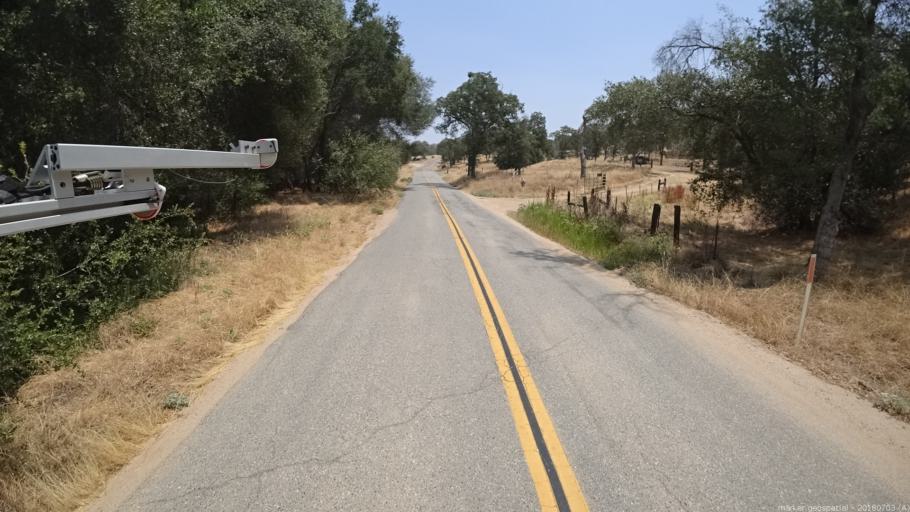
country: US
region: California
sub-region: Madera County
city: Yosemite Lakes
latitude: 37.0603
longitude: -119.6848
